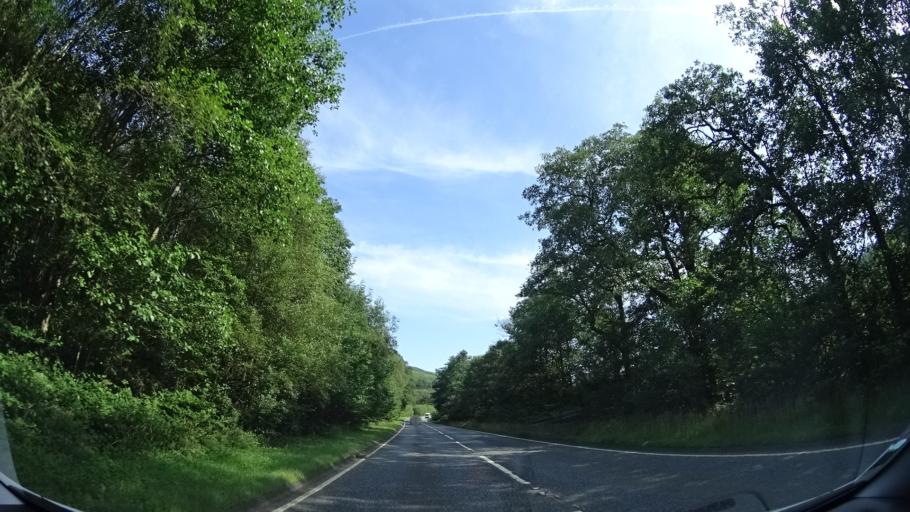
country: GB
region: Scotland
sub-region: Argyll and Bute
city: Garelochhead
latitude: 56.3463
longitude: -4.7037
